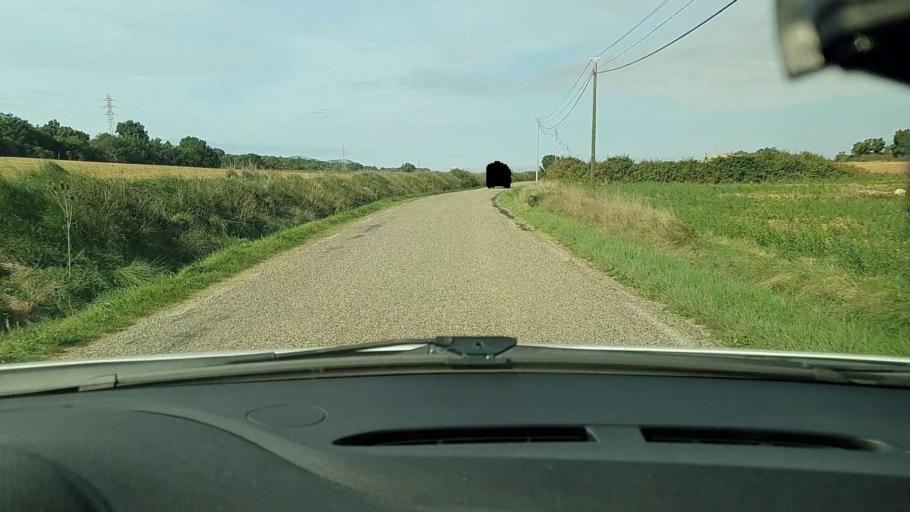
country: FR
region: Languedoc-Roussillon
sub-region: Departement du Gard
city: Goudargues
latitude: 44.1448
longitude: 4.3842
